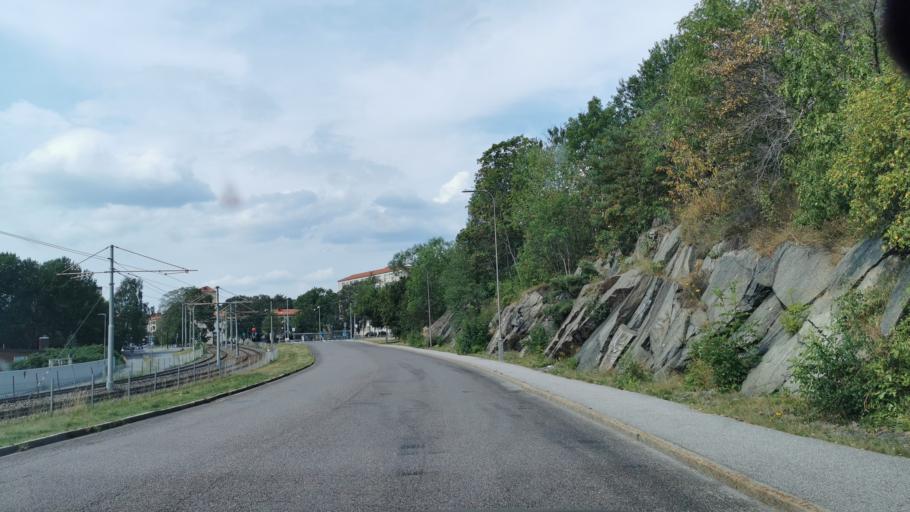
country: SE
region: Vaestra Goetaland
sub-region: Goteborg
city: Goeteborg
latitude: 57.6875
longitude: 11.9707
